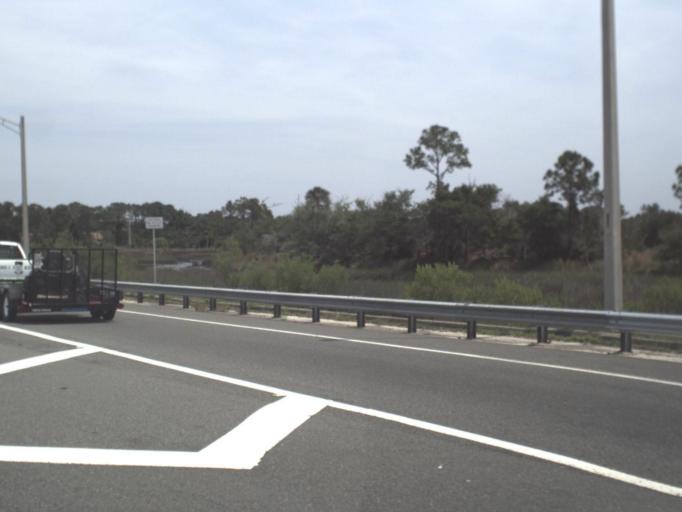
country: US
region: Florida
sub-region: Duval County
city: Atlantic Beach
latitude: 30.3242
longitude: -81.4271
